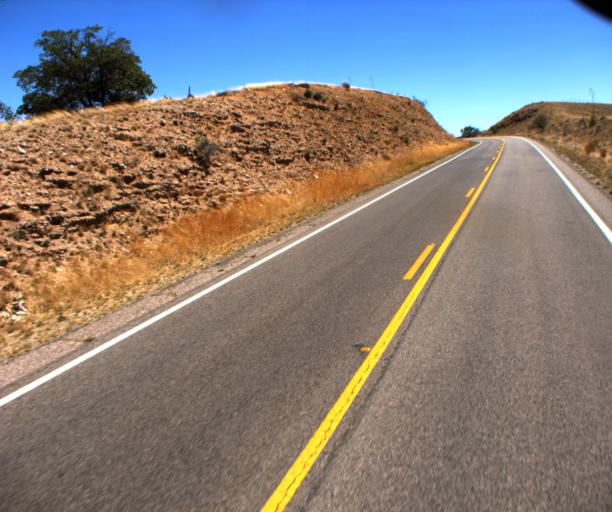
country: US
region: Arizona
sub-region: Pima County
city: Corona de Tucson
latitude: 31.8064
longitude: -110.7084
